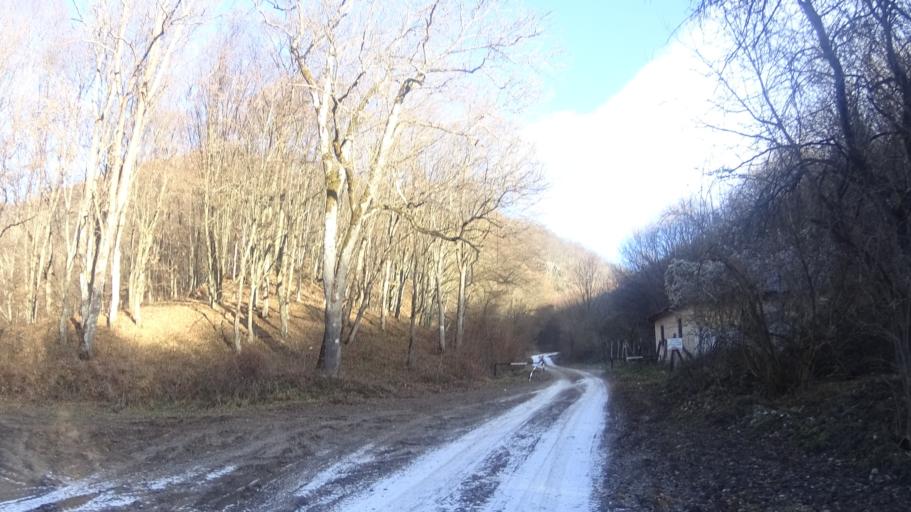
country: HU
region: Borsod-Abauj-Zemplen
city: Bogacs
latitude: 48.0214
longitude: 20.5402
